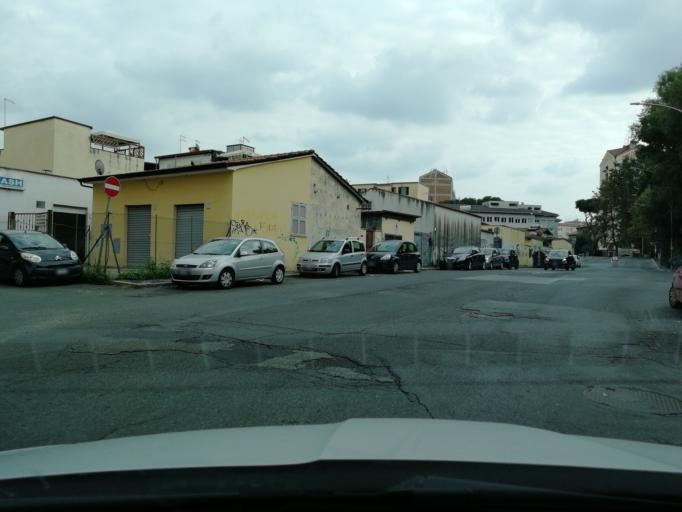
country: IT
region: Latium
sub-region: Citta metropolitana di Roma Capitale
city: Rome
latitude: 41.8608
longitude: 12.5501
